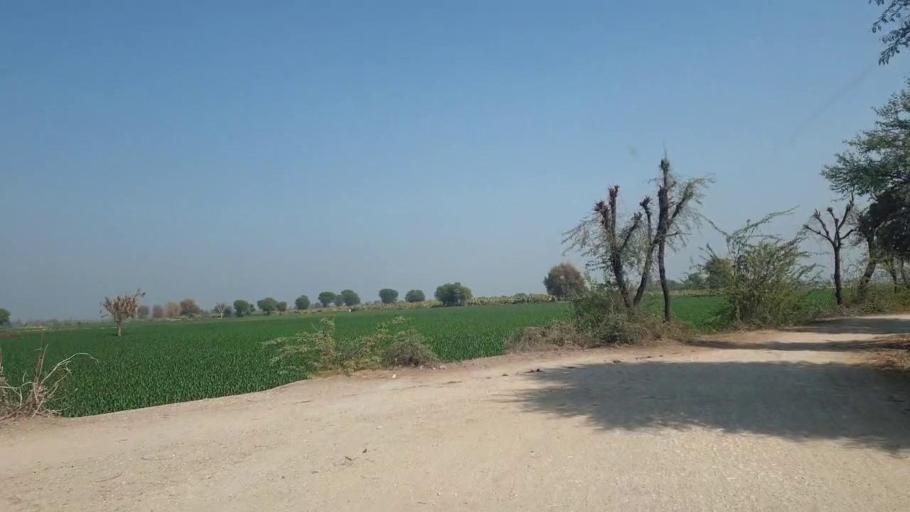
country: PK
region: Sindh
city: Sakrand
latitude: 26.0498
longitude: 68.4340
